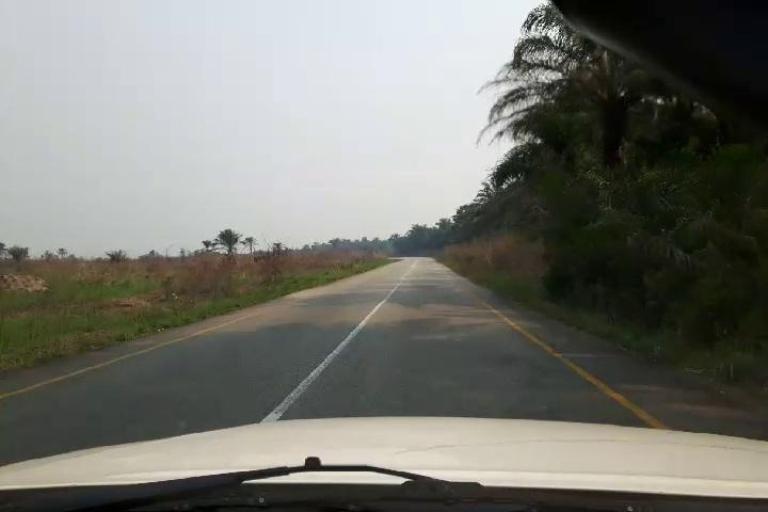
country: SL
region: Southern Province
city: Largo
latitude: 8.2162
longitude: -12.0742
